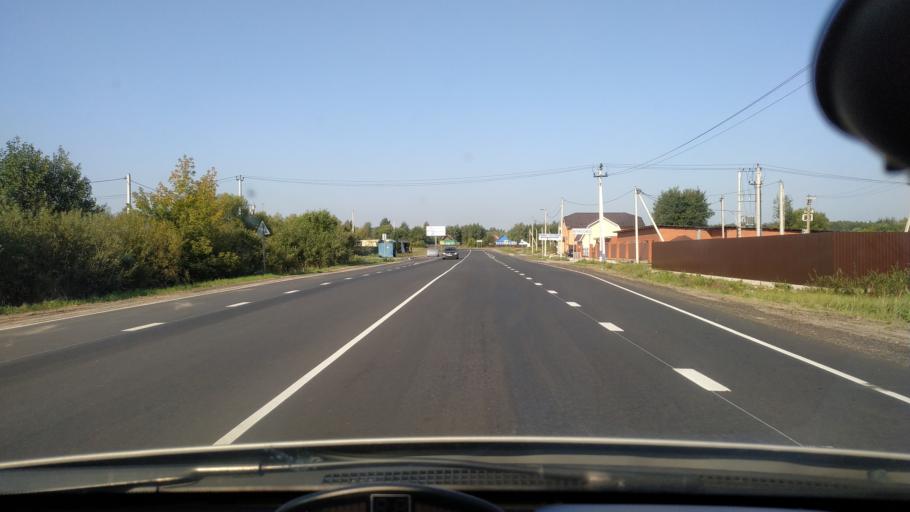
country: RU
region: Moskovskaya
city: Misheronskiy
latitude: 55.6577
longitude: 39.7560
